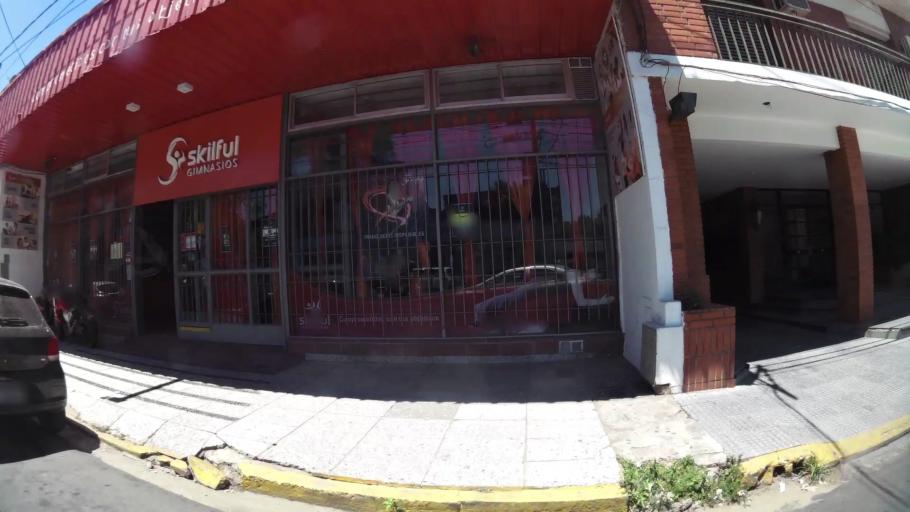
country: AR
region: Santa Fe
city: Santa Fe de la Vera Cruz
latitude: -31.6436
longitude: -60.7083
